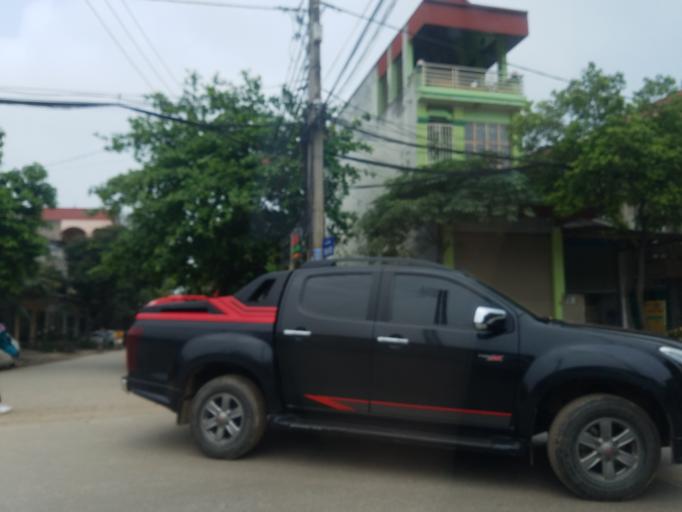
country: VN
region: Thai Nguyen
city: Chua Hang
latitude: 21.6207
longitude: 105.8399
